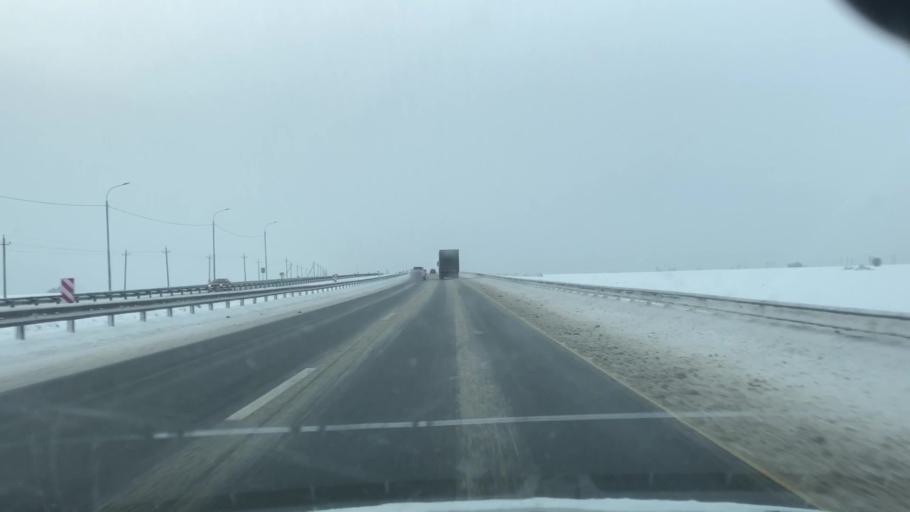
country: RU
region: Moskovskaya
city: Mikhnevo
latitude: 55.1106
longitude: 37.9261
